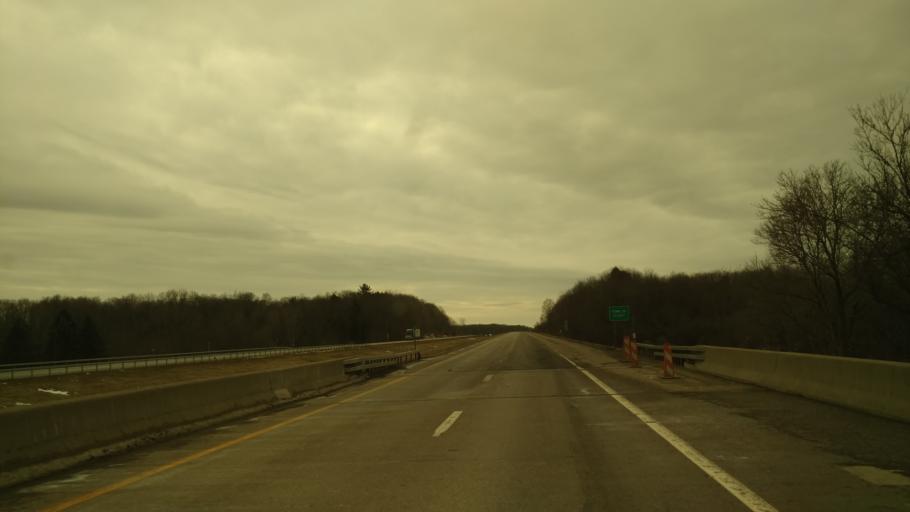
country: US
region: New York
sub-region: Chautauqua County
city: Celoron
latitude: 42.1283
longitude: -79.2951
